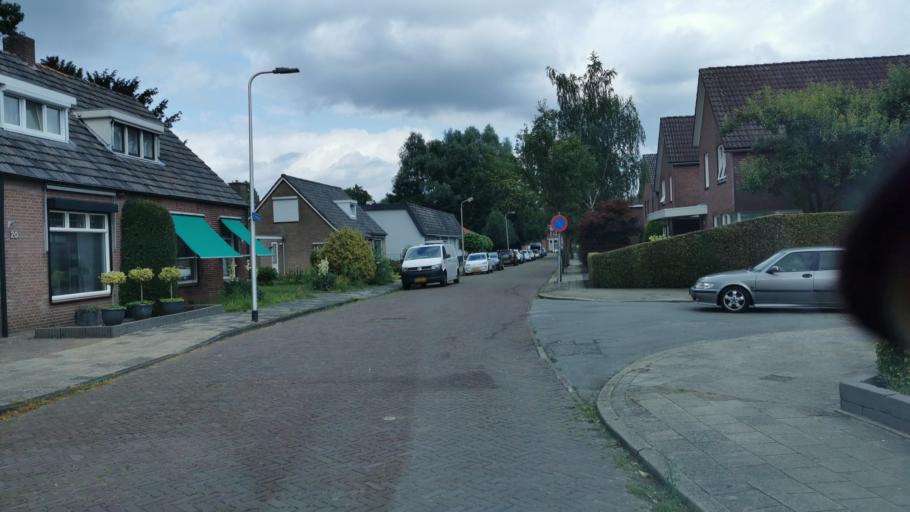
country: NL
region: Overijssel
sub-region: Gemeente Losser
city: Losser
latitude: 52.2621
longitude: 7.0023
